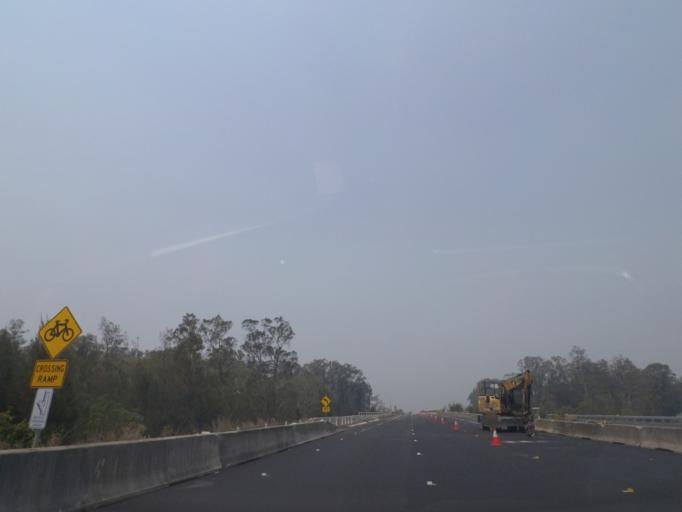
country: AU
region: New South Wales
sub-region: Ballina
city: Ballina
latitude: -28.8665
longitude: 153.4965
